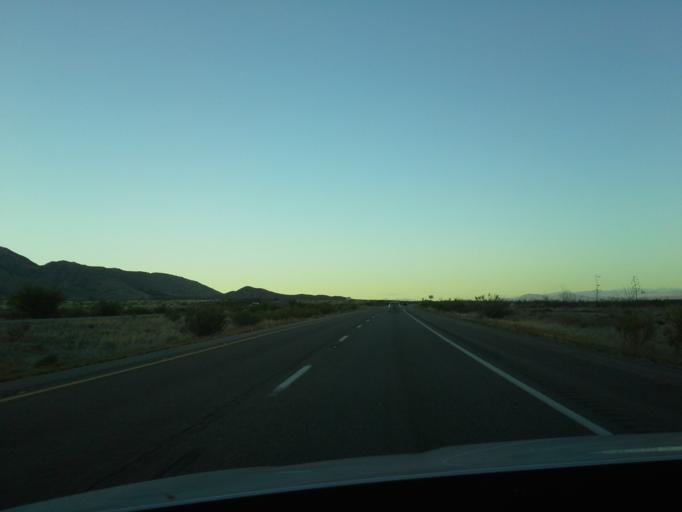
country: US
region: Arizona
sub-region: Cochise County
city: Whetstone
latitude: 31.8030
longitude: -110.3497
